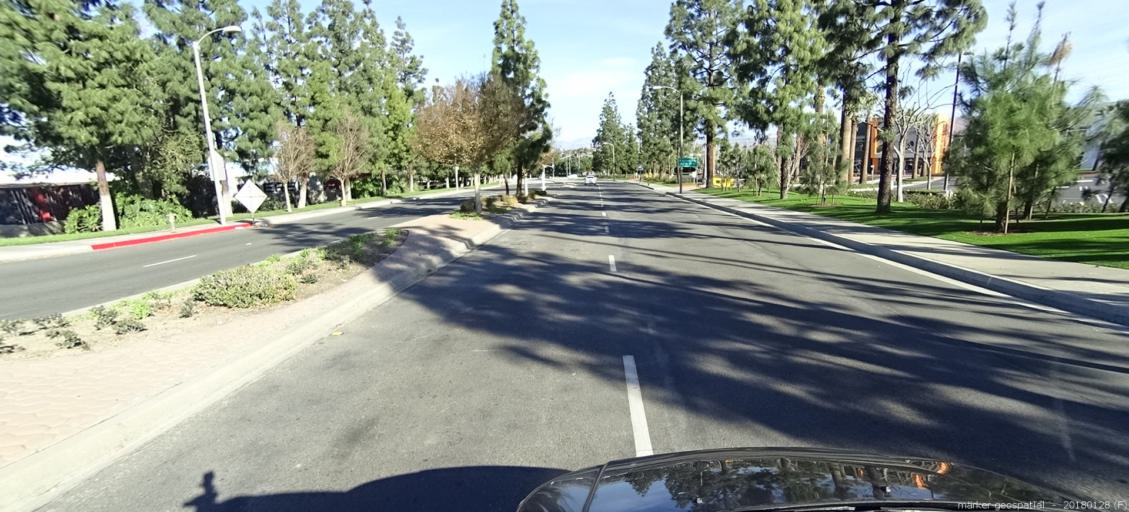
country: US
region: California
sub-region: Los Angeles County
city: Walnut
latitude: 34.0038
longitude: -117.8552
